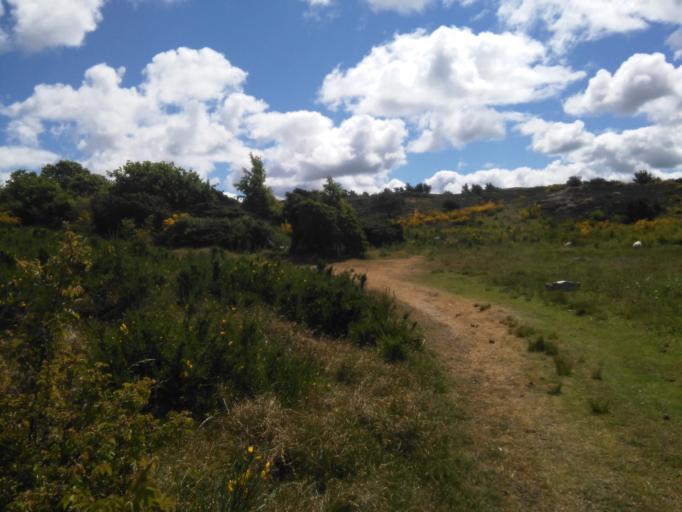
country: DK
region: Capital Region
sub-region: Bornholm Kommune
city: Ronne
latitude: 55.2930
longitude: 14.7683
